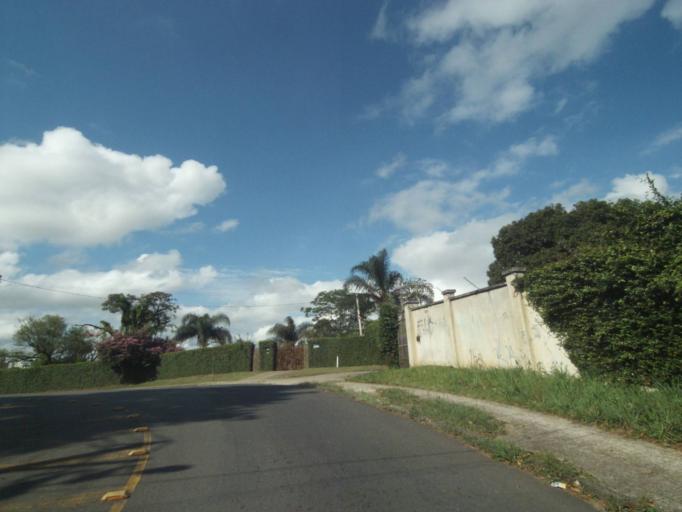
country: BR
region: Parana
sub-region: Curitiba
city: Curitiba
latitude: -25.3844
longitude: -49.3035
